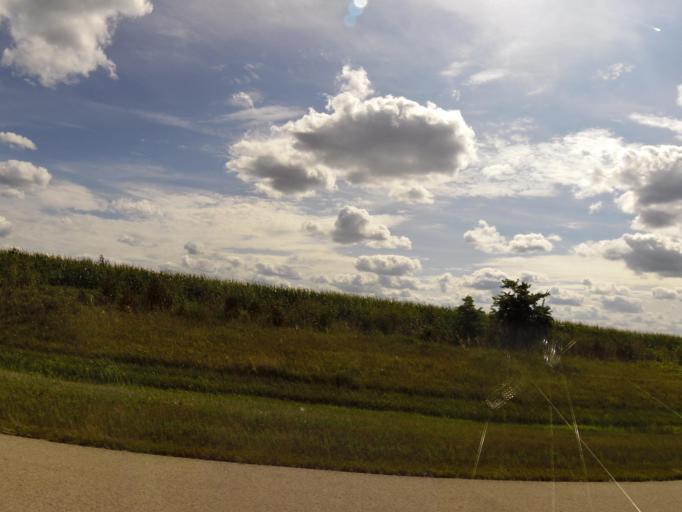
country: US
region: Illinois
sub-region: Ogle County
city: Rochelle
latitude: 41.9054
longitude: -88.9738
